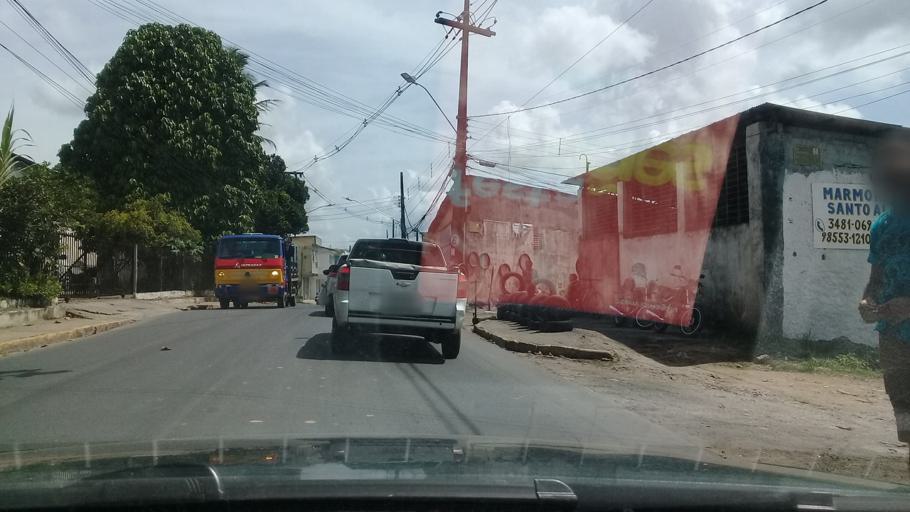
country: BR
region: Pernambuco
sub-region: Jaboatao Dos Guararapes
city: Jaboatao dos Guararapes
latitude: -8.0938
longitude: -35.0222
